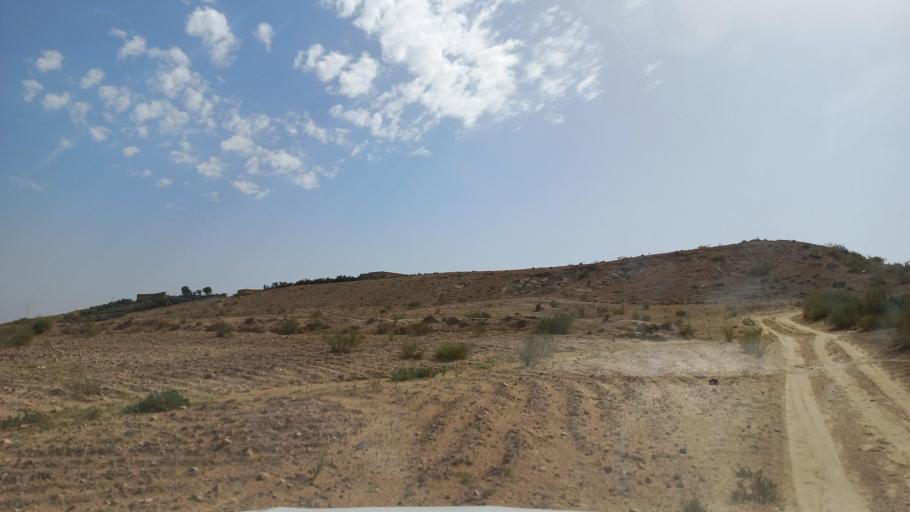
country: TN
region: Al Qasrayn
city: Kasserine
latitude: 35.2792
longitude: 8.9726
